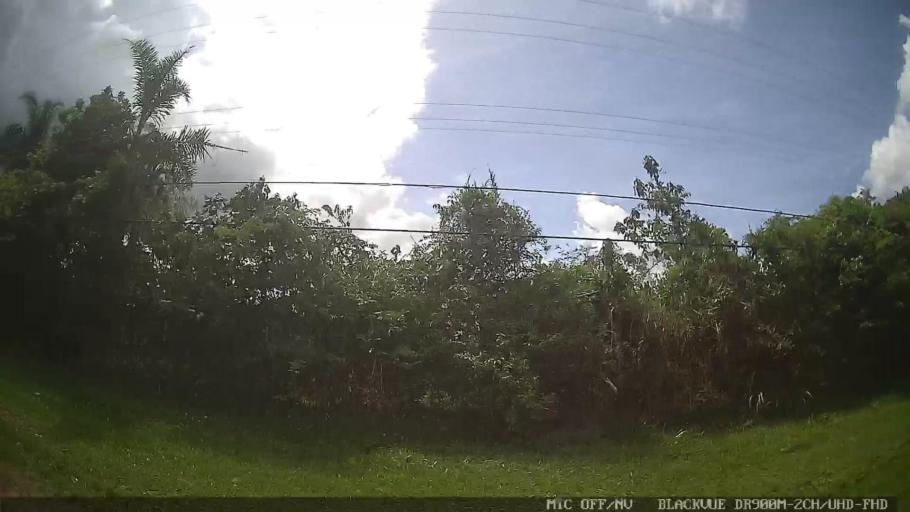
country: BR
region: Sao Paulo
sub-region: Suzano
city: Suzano
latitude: -23.6613
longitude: -46.2437
